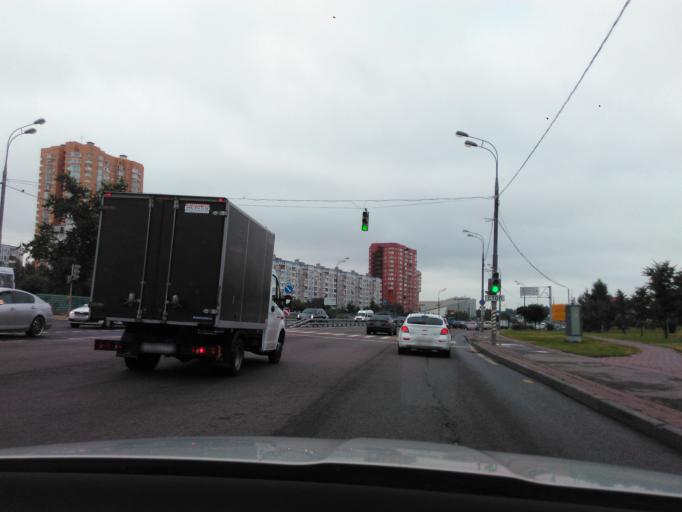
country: RU
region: Moscow
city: Khimki
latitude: 55.8921
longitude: 37.4036
